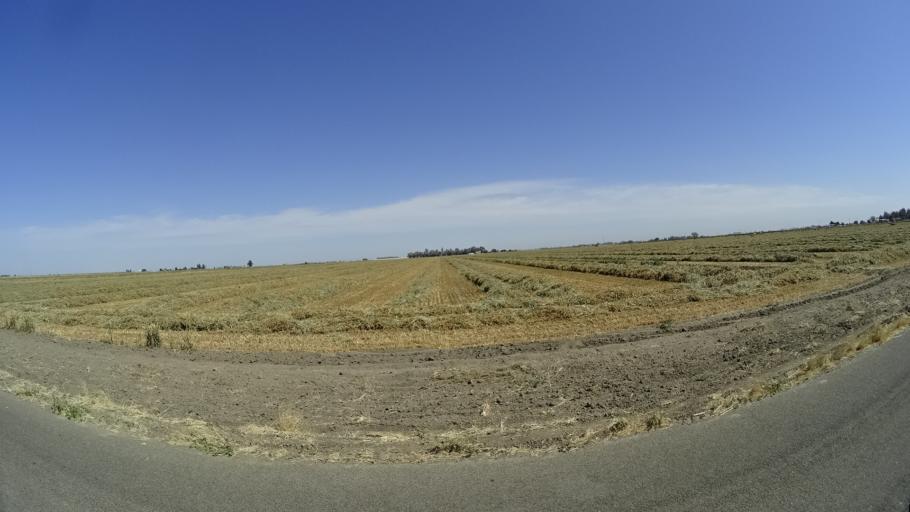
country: US
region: California
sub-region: Kings County
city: Stratford
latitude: 36.1967
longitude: -119.8058
